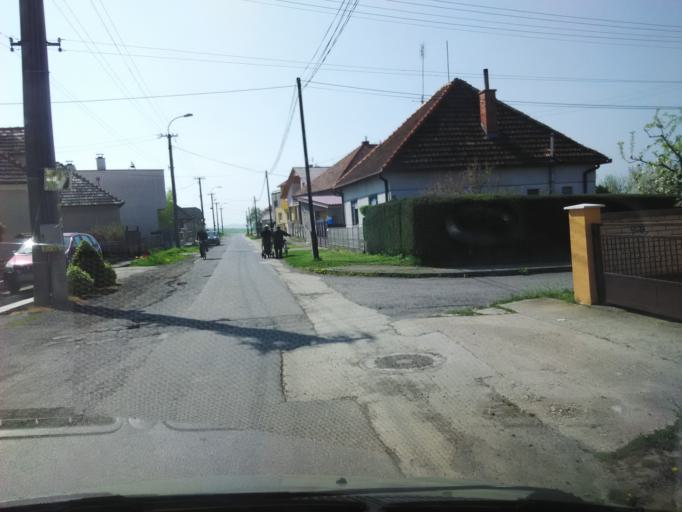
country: SK
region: Nitriansky
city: Tlmace
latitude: 48.2874
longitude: 18.6023
